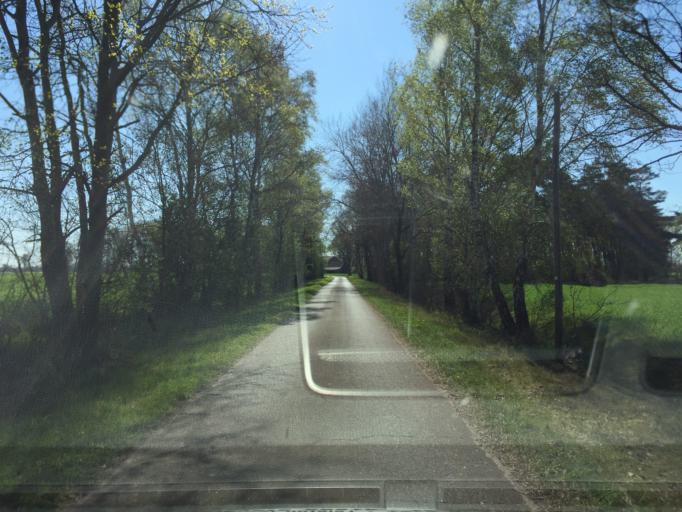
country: DE
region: Lower Saxony
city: Wehrbleck
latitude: 52.5698
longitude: 8.6862
